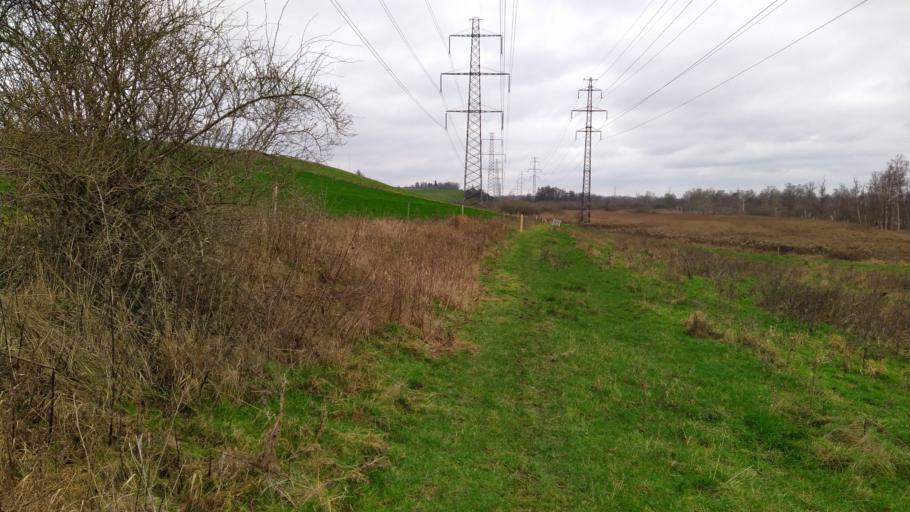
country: DK
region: Capital Region
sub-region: Egedal Kommune
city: Stenlose
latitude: 55.7607
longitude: 12.2122
